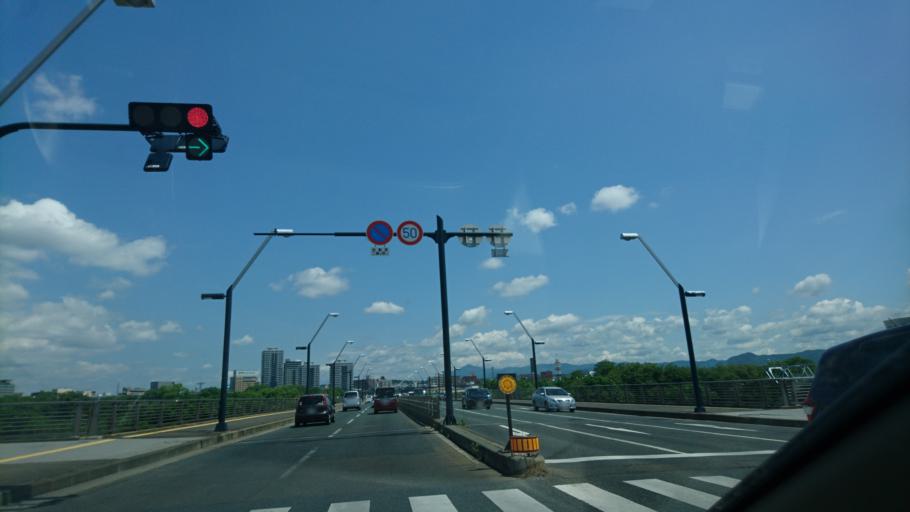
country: JP
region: Iwate
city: Morioka-shi
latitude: 39.6922
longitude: 141.1369
